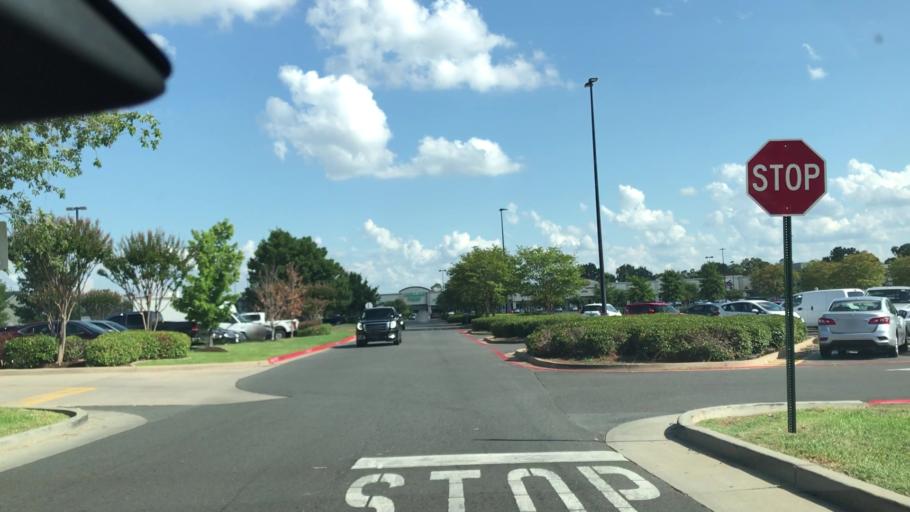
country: US
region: Louisiana
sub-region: Bossier Parish
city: Bossier City
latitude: 32.4394
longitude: -93.7181
